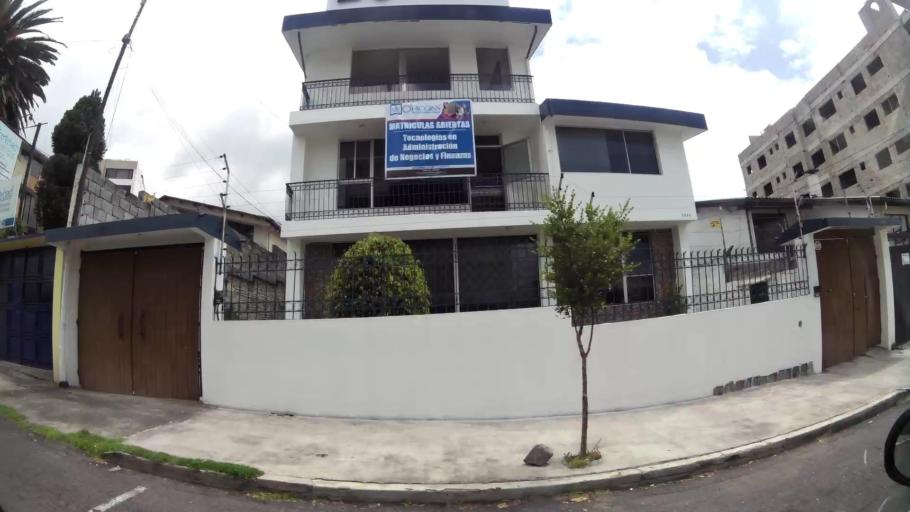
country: EC
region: Pichincha
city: Quito
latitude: -0.1803
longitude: -78.4935
